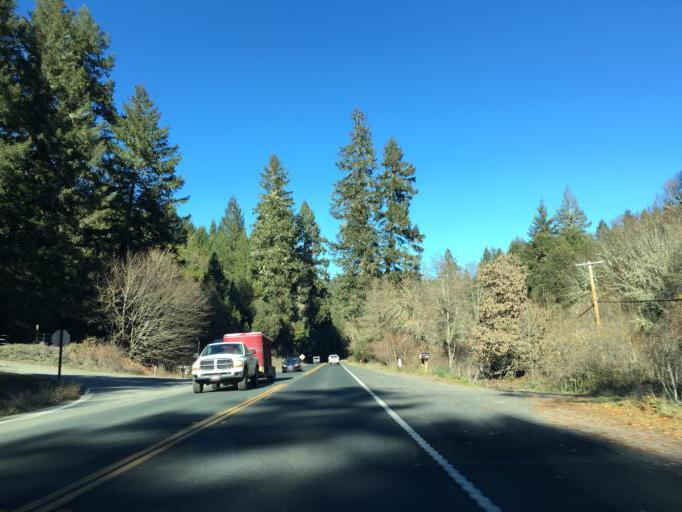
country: US
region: California
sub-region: Mendocino County
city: Brooktrails
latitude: 39.4829
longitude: -123.3614
